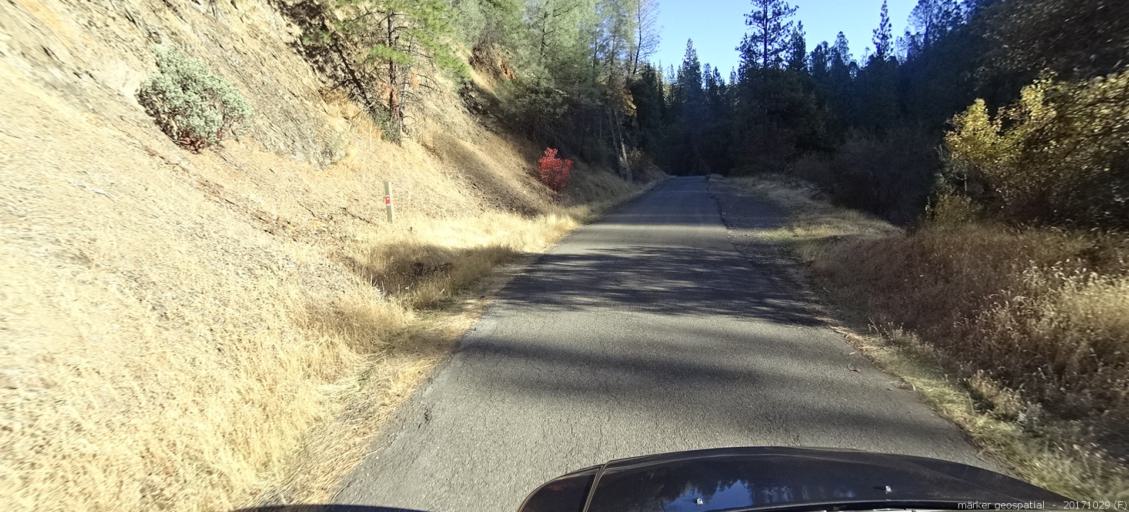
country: US
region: California
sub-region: Trinity County
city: Hayfork
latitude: 40.3905
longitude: -122.9865
